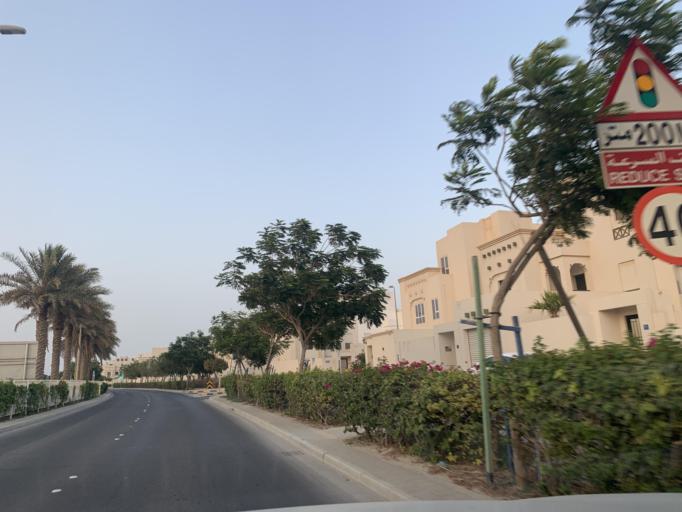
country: BH
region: Manama
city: Jidd Hafs
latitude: 26.2249
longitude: 50.4470
